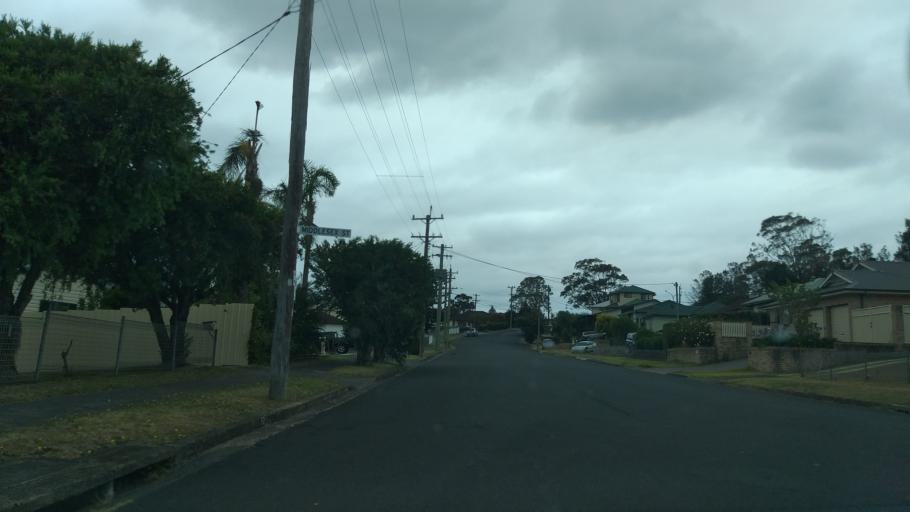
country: AU
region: New South Wales
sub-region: Wollongong
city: Berkeley
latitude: -34.4830
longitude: 150.8415
